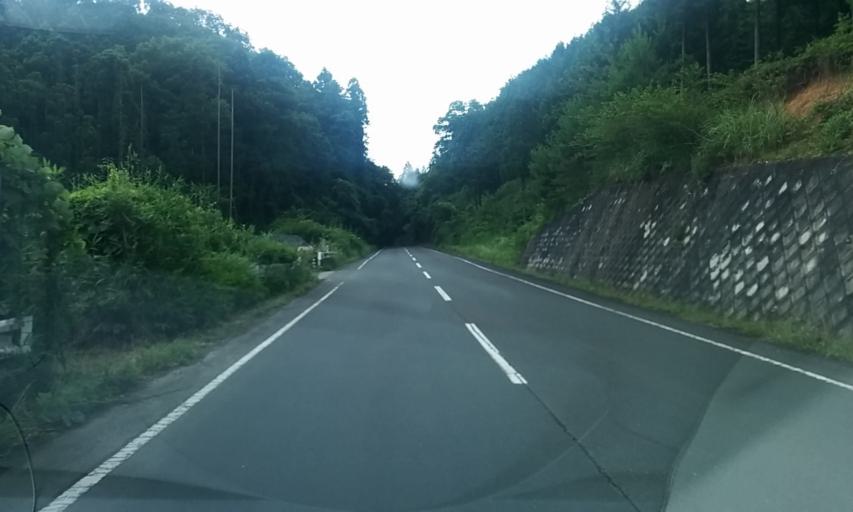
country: JP
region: Kyoto
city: Kameoka
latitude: 35.0910
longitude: 135.4324
